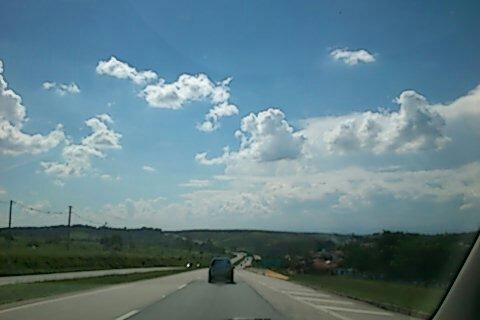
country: BR
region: Sao Paulo
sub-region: Sao Jose Dos Campos
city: Sao Jose dos Campos
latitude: -23.2598
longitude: -45.8321
